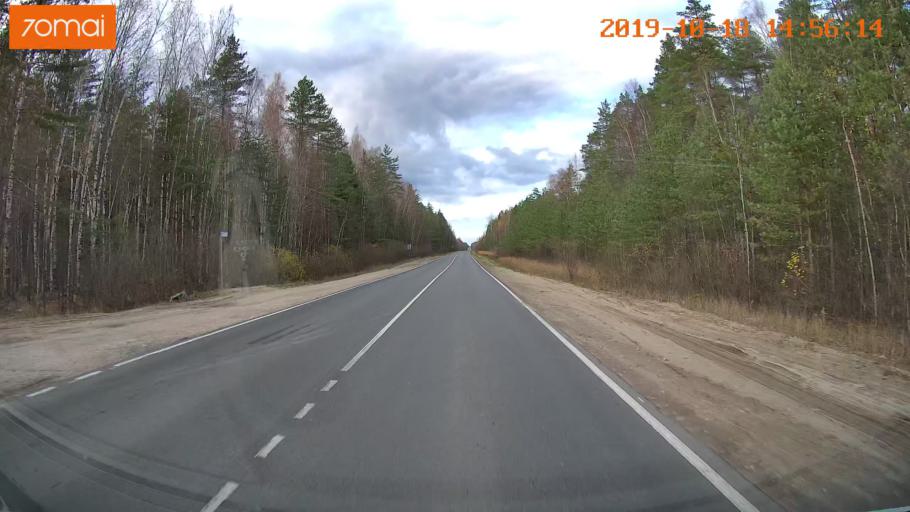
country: RU
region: Vladimir
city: Kurlovo
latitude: 55.4619
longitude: 40.5885
